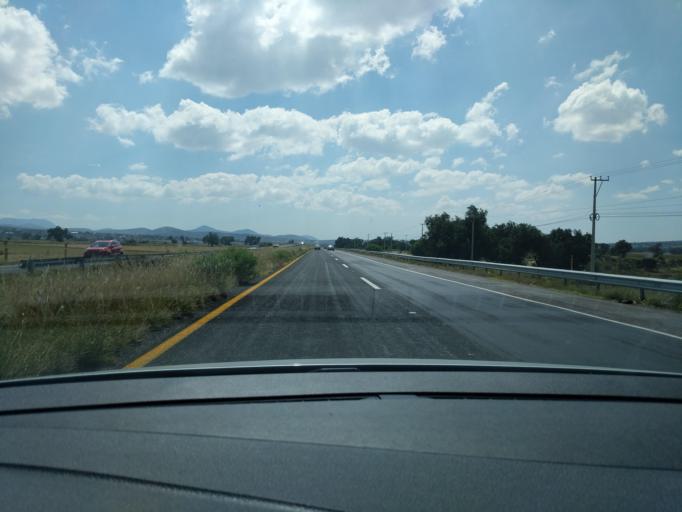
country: MX
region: Hidalgo
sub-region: Mineral de la Reforma
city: Rinconada de los Angeles
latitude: 19.9732
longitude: -98.6996
